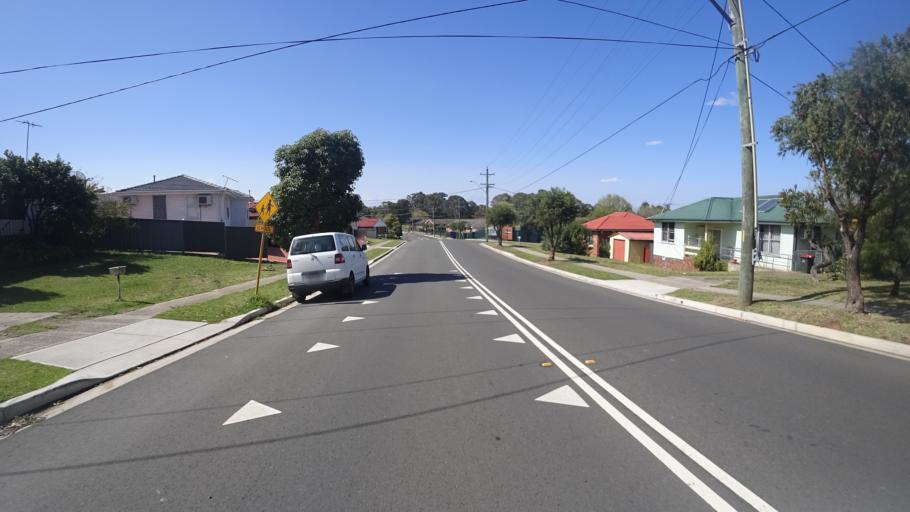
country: AU
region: New South Wales
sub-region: Fairfield
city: Cabramatta West
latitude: -33.9055
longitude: 150.9102
